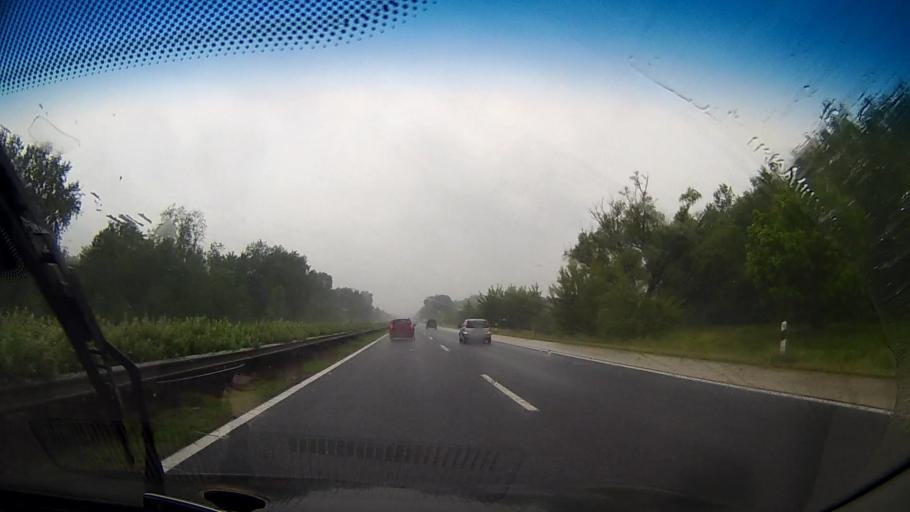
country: HU
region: Komarom-Esztergom
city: Vertesszolos
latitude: 47.6078
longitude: 18.3670
